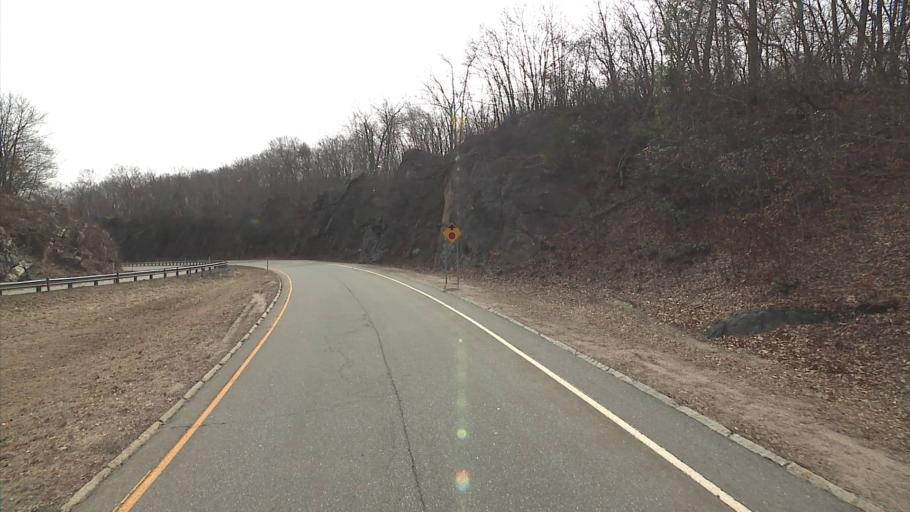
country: US
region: Connecticut
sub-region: Middlesex County
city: Deep River Center
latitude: 41.3609
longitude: -72.4260
